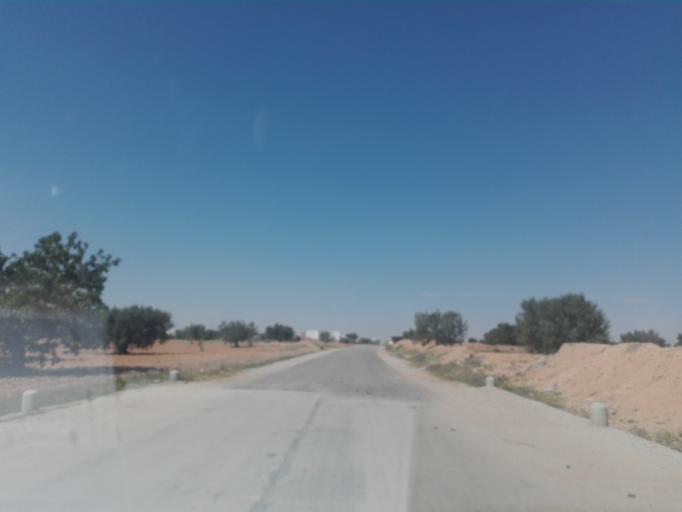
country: TN
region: Safaqis
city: Bi'r `Ali Bin Khalifah
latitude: 34.6697
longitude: 10.3640
